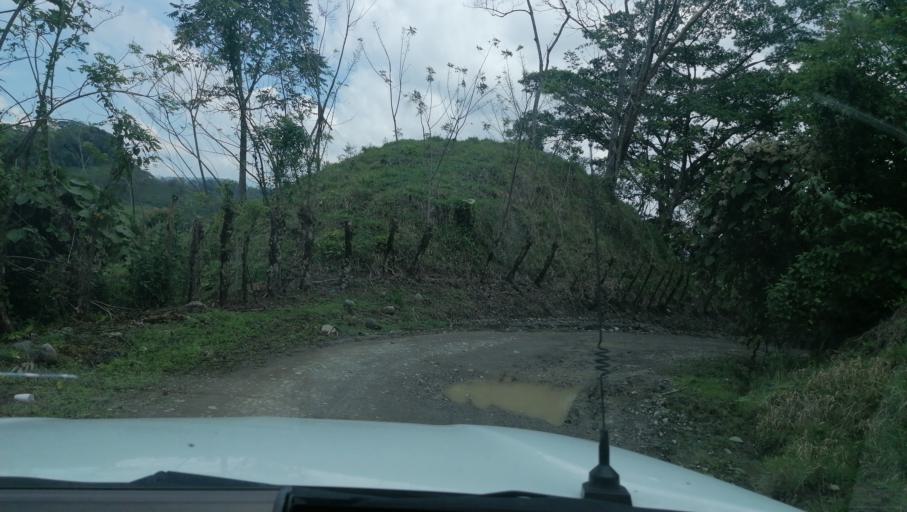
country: MX
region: Chiapas
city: Ixtacomitan
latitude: 17.4401
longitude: -93.2021
